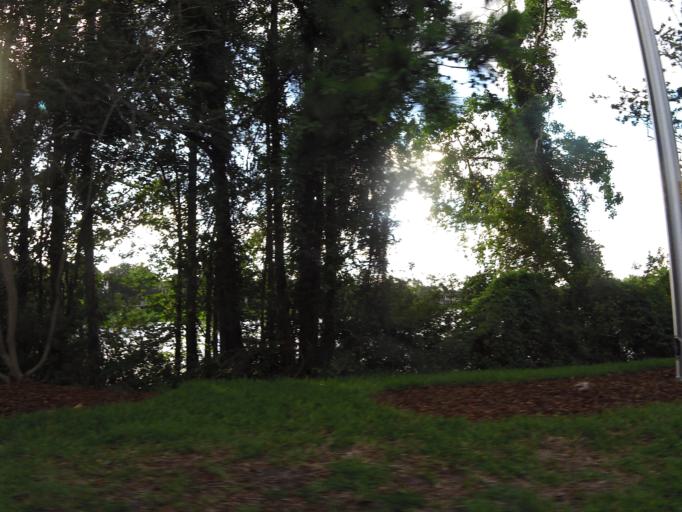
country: US
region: Florida
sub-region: Duval County
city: Jacksonville
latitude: 30.2523
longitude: -81.5391
